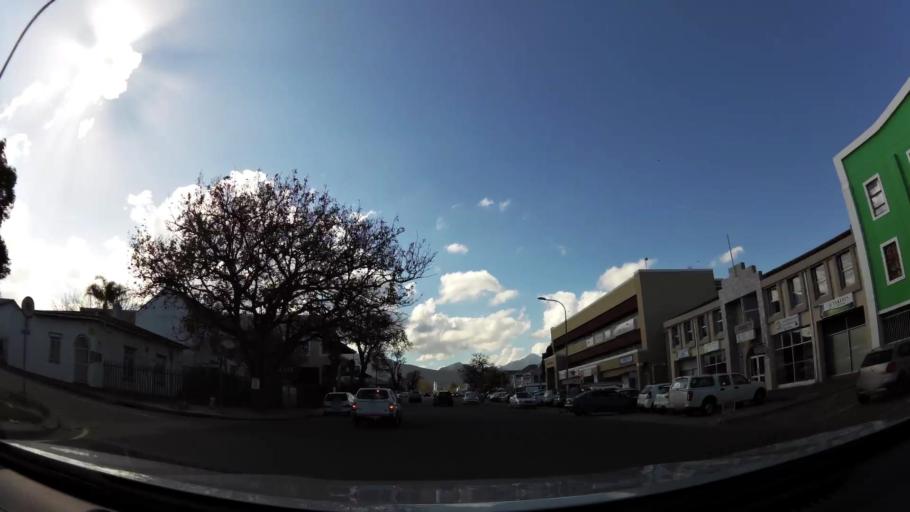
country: ZA
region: Western Cape
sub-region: Eden District Municipality
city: George
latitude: -33.9629
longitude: 22.4578
